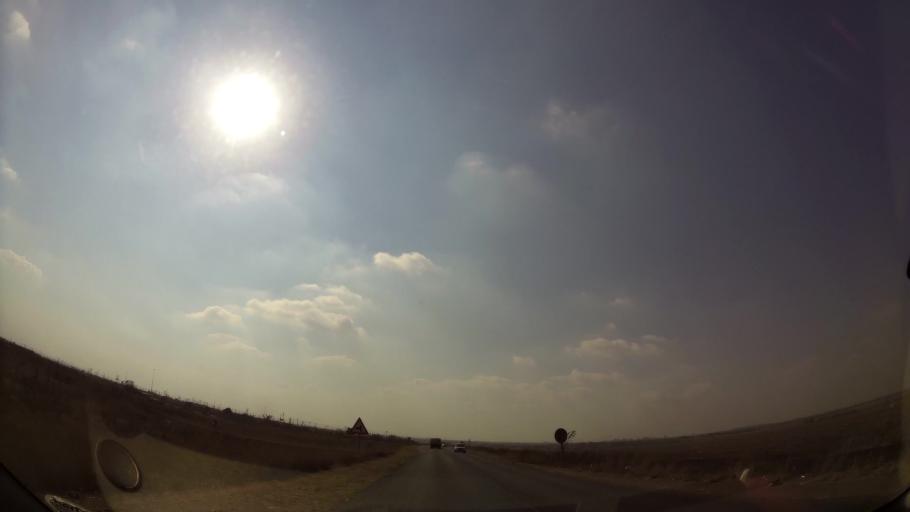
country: ZA
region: Gauteng
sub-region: Ekurhuleni Metropolitan Municipality
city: Springs
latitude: -26.1405
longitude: 28.4505
